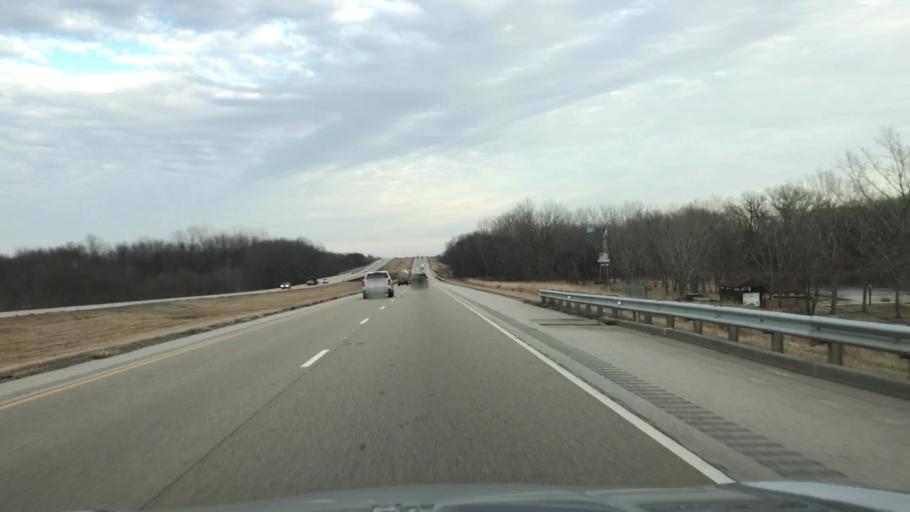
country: US
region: Illinois
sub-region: Logan County
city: Lincoln
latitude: 40.1814
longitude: -89.3750
